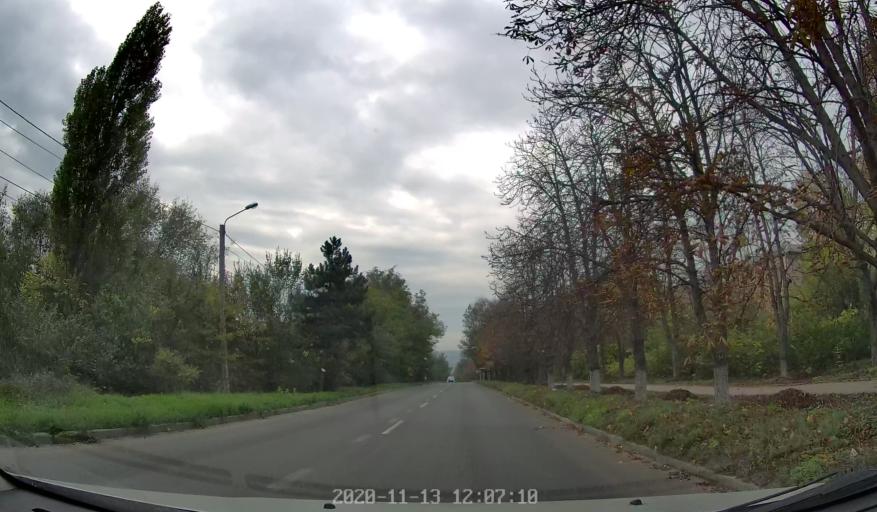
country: MD
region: Chisinau
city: Chisinau
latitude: 46.9766
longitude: 28.8363
